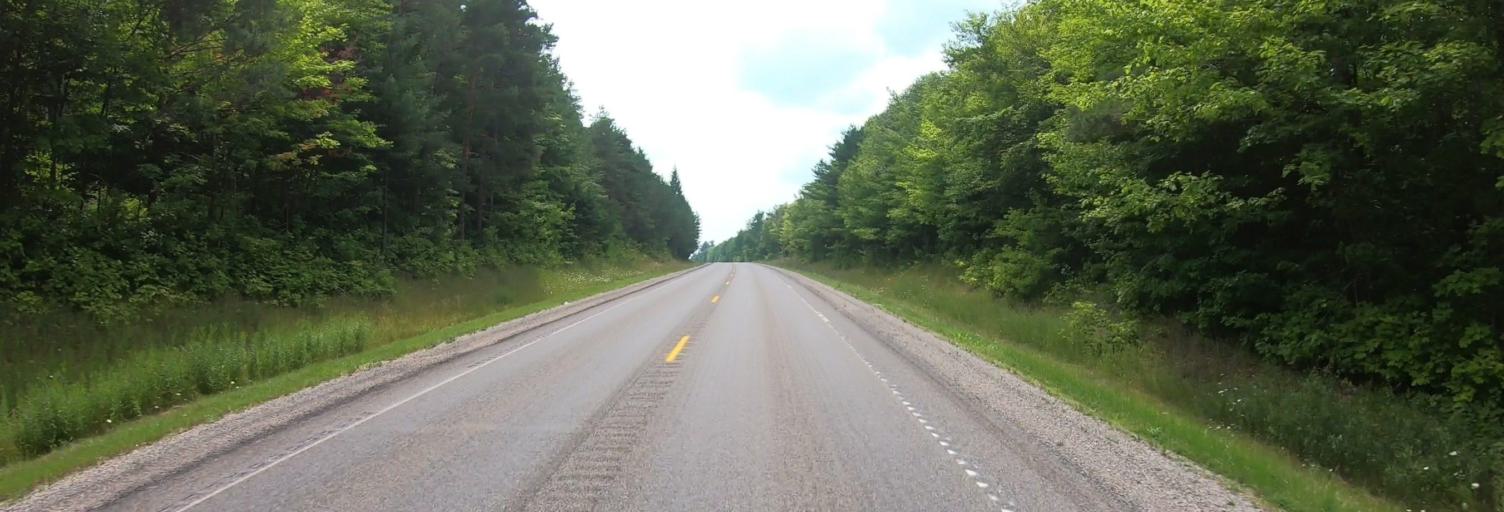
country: US
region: Michigan
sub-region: Alger County
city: Munising
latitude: 46.3567
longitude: -86.7201
